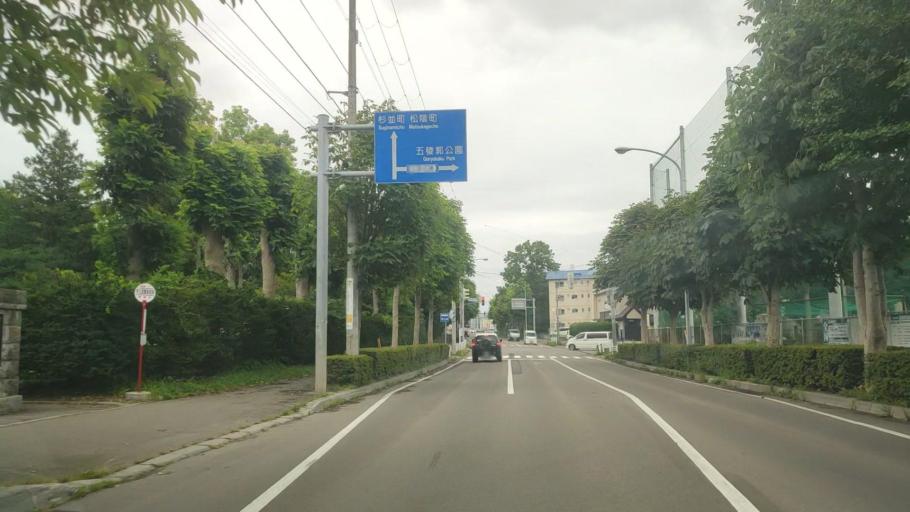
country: JP
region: Hokkaido
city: Hakodate
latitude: 41.7944
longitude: 140.7614
